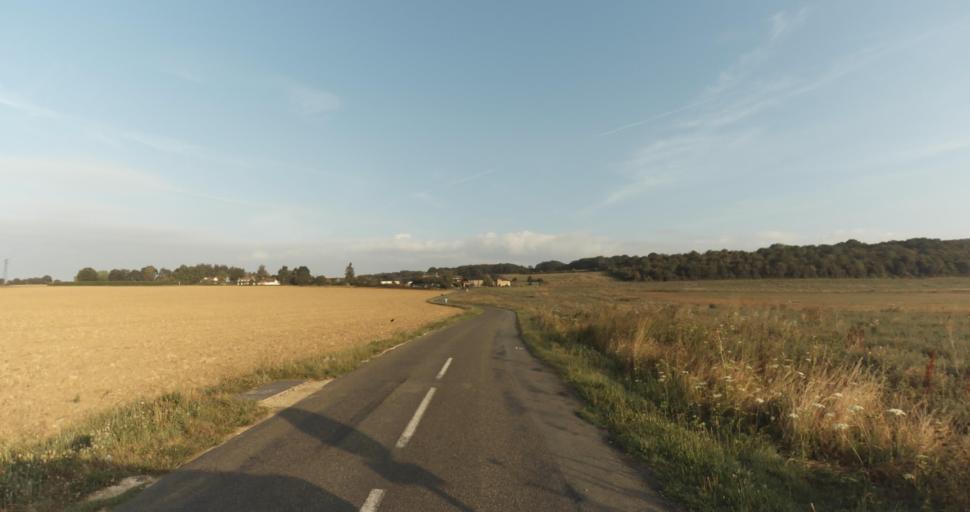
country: FR
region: Centre
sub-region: Departement d'Eure-et-Loir
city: Vert-en-Drouais
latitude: 48.7755
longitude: 1.3365
